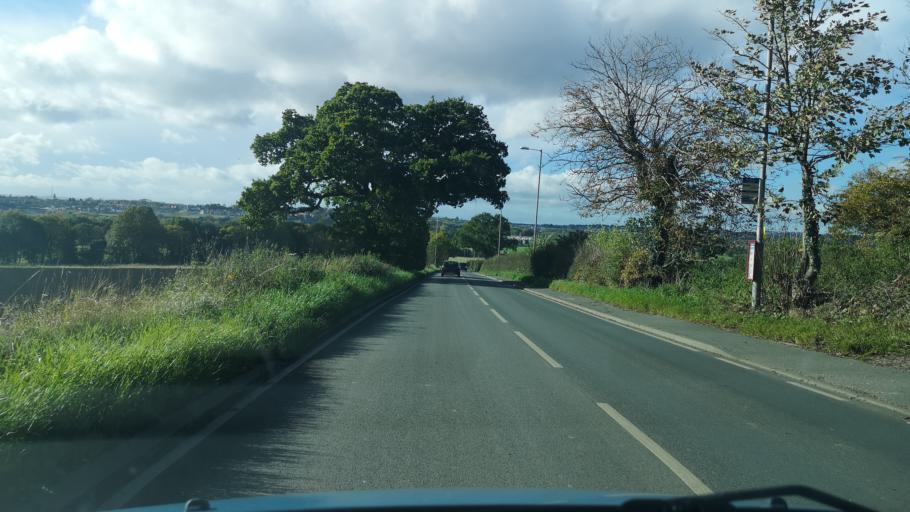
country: GB
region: England
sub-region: City and Borough of Wakefield
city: Normanton
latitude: 53.7053
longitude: -1.4525
